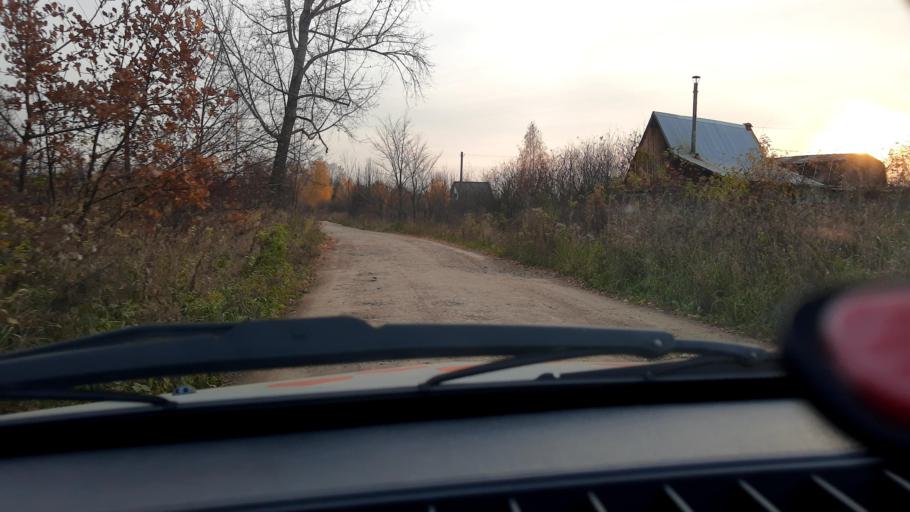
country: RU
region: Bashkortostan
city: Iglino
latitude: 54.7982
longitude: 56.3399
